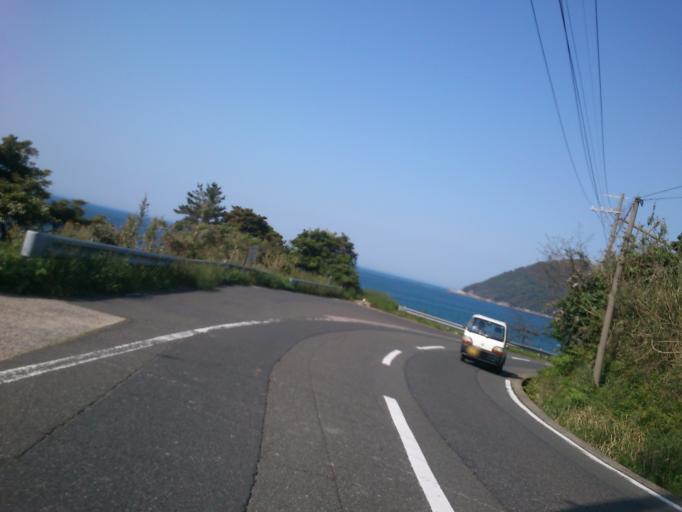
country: JP
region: Kyoto
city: Miyazu
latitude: 35.7641
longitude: 135.1992
